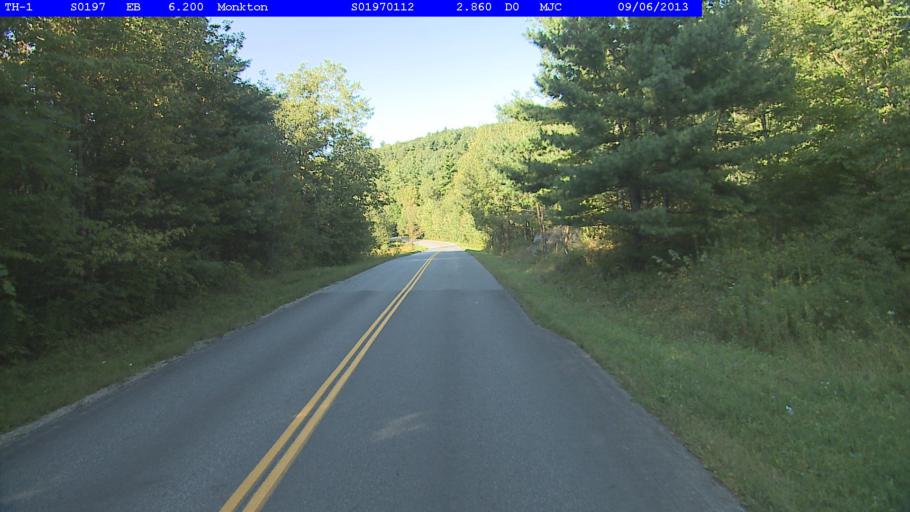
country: US
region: Vermont
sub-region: Addison County
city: Vergennes
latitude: 44.2190
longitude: -73.1540
